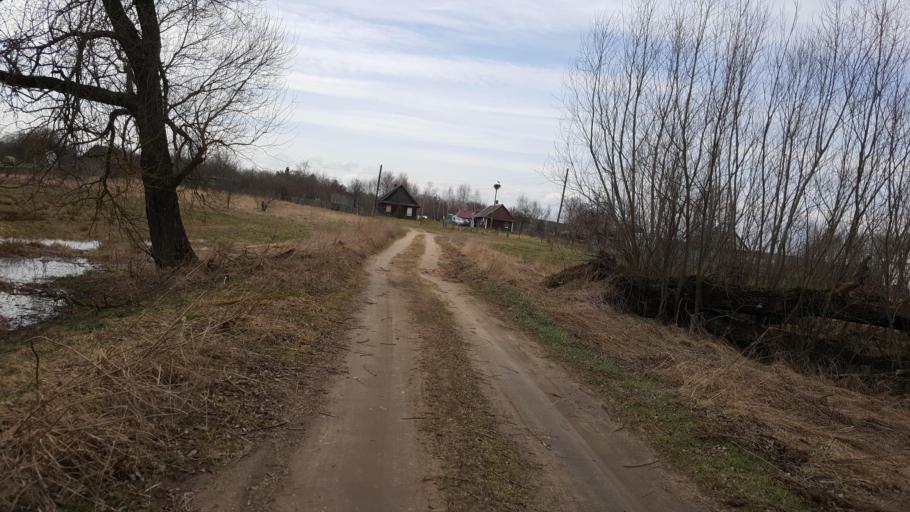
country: BY
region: Brest
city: Kamyanyets
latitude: 52.3742
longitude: 23.9785
